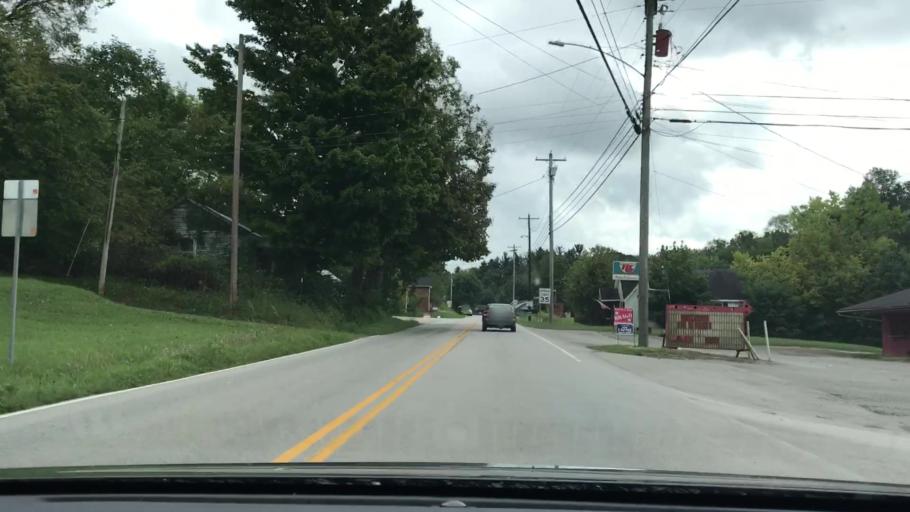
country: US
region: Kentucky
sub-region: Metcalfe County
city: Edmonton
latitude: 36.8853
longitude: -85.7061
